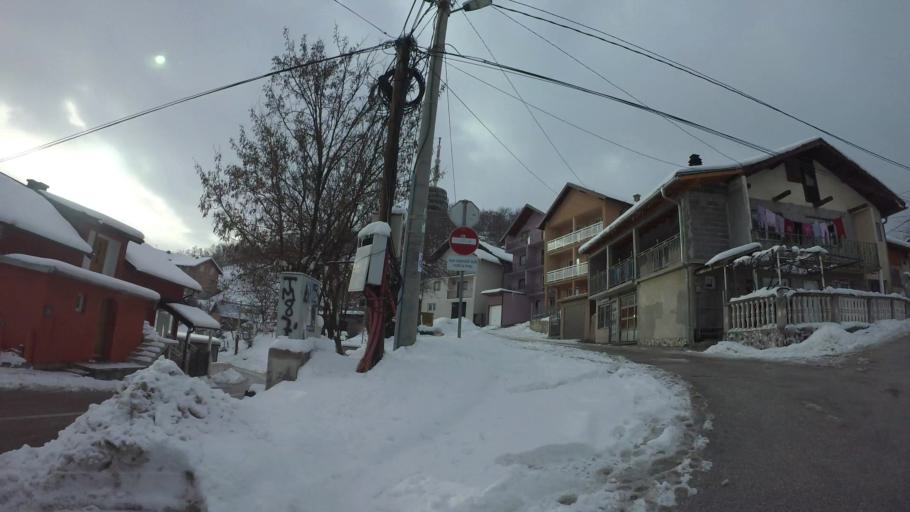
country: BA
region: Federation of Bosnia and Herzegovina
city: Kobilja Glava
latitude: 43.8727
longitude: 18.3899
